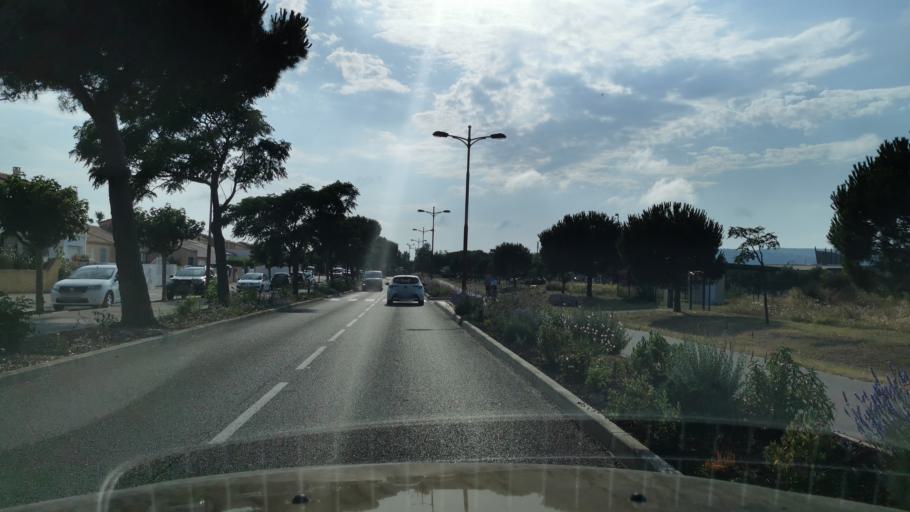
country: FR
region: Languedoc-Roussillon
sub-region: Departement de l'Aude
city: Gruissan
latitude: 43.1171
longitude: 3.1156
